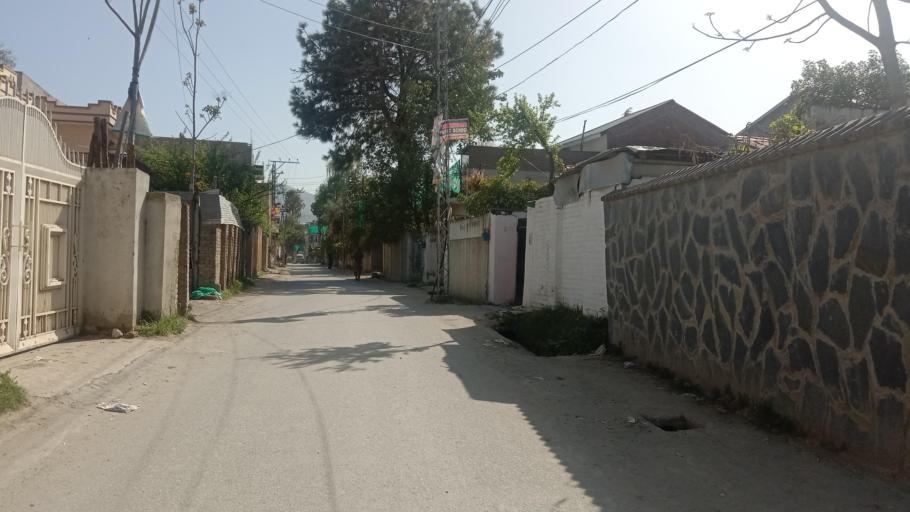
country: PK
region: Khyber Pakhtunkhwa
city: Abbottabad
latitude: 34.1751
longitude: 73.2244
